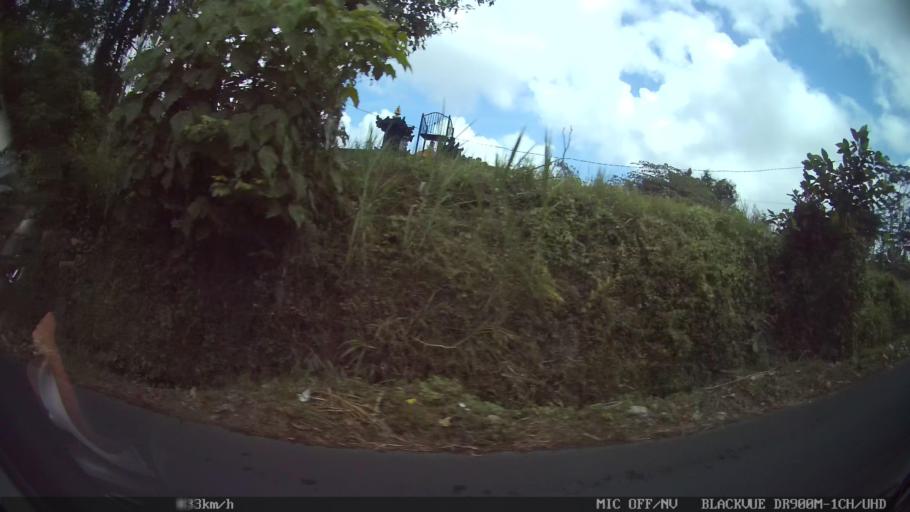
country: ID
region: Bali
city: Banjar Desa
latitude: -8.5851
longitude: 115.2874
